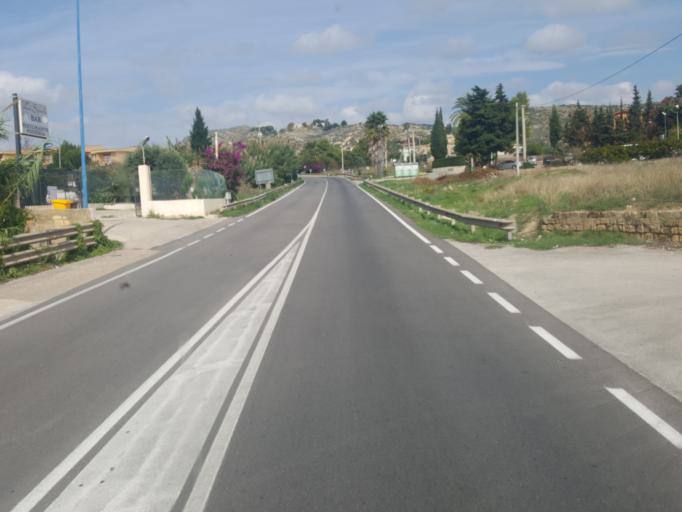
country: IT
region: Sicily
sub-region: Agrigento
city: Porto Empedocle
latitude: 37.2953
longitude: 13.4973
